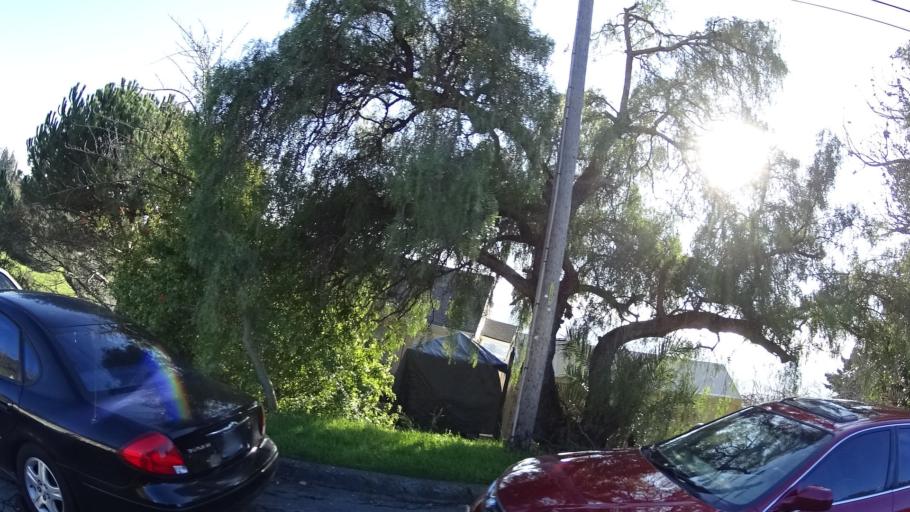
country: US
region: California
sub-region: Alameda County
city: Hayward
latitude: 37.6558
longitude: -122.0645
